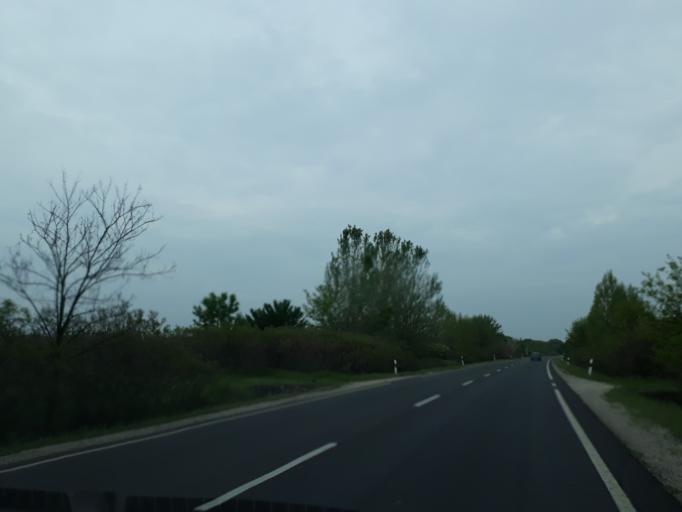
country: HU
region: Szabolcs-Szatmar-Bereg
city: Demecser
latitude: 48.0702
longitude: 21.9511
